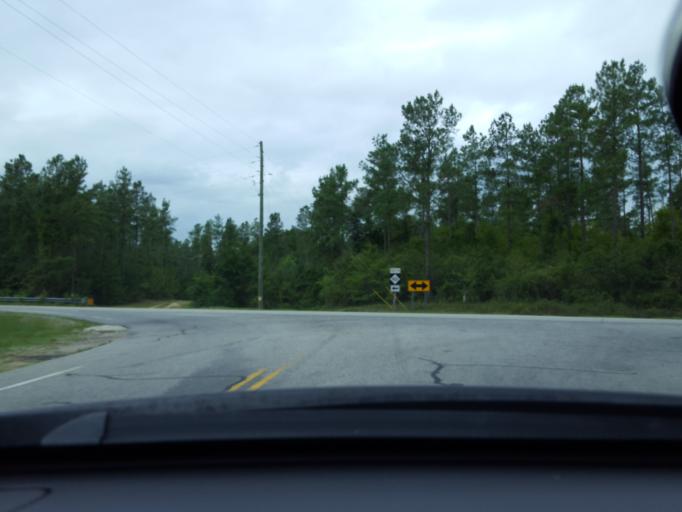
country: US
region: North Carolina
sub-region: Sampson County
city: Clinton
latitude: 34.7887
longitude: -78.3227
